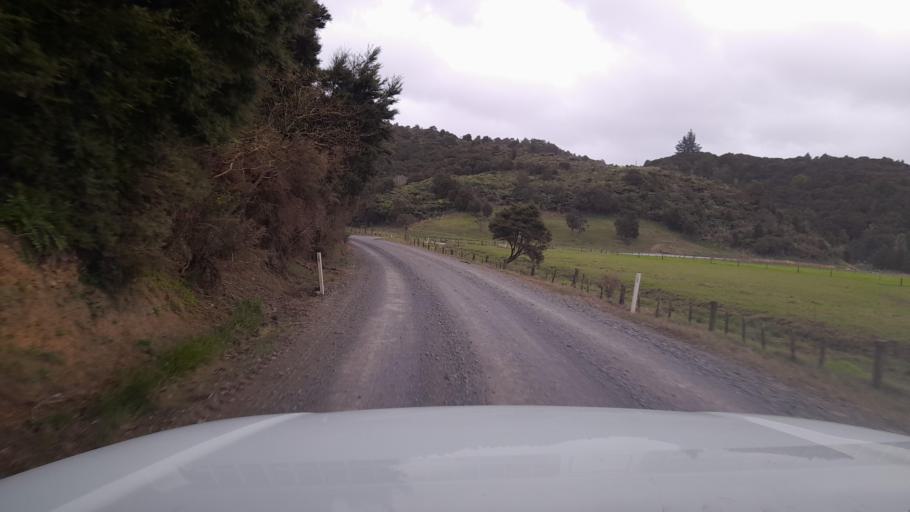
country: NZ
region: Northland
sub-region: Far North District
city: Paihia
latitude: -35.3433
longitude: 174.2297
